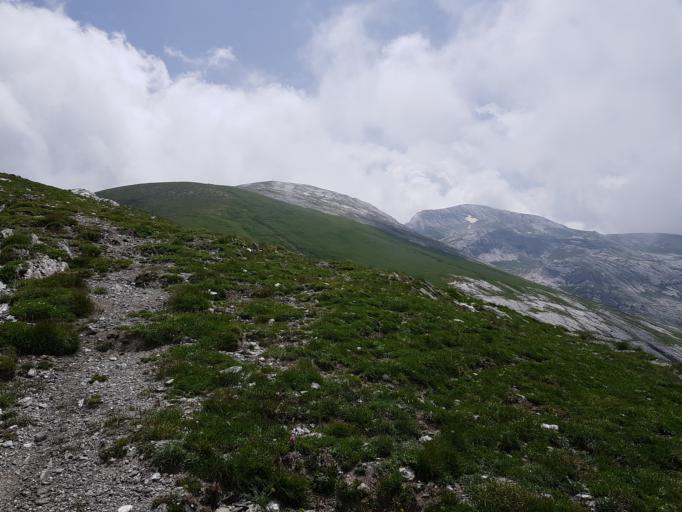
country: IT
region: Piedmont
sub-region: Provincia di Cuneo
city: Frabosa Soprana
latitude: 44.1894
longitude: 7.7715
